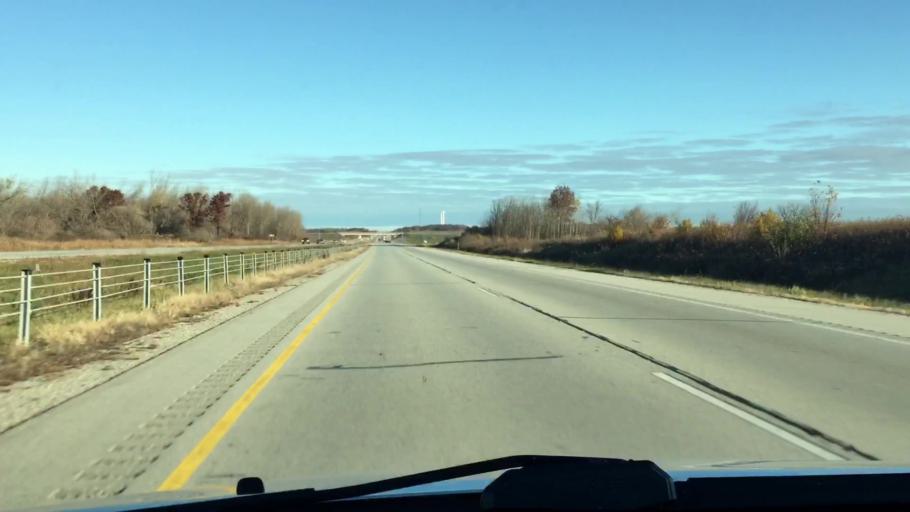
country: US
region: Wisconsin
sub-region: Dodge County
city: Lomira
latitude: 43.6293
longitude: -88.4409
